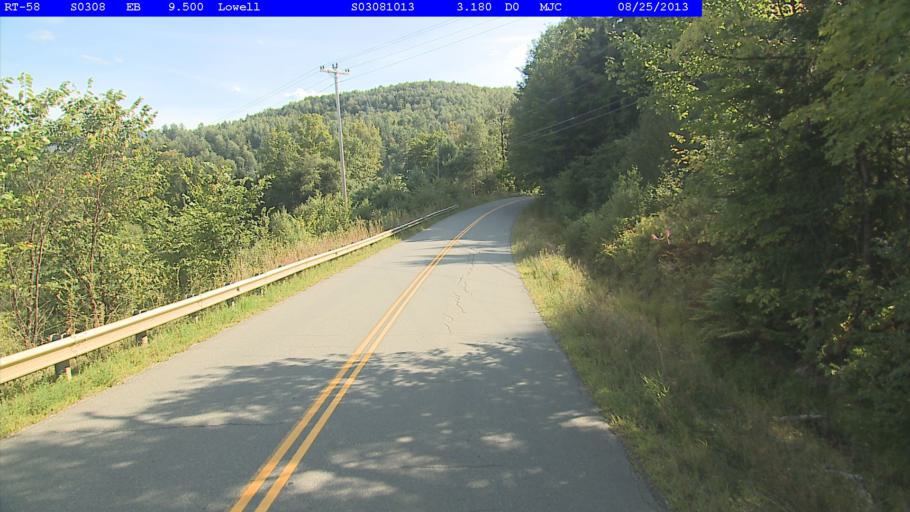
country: US
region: Vermont
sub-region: Lamoille County
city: Hyde Park
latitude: 44.8081
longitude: -72.4600
